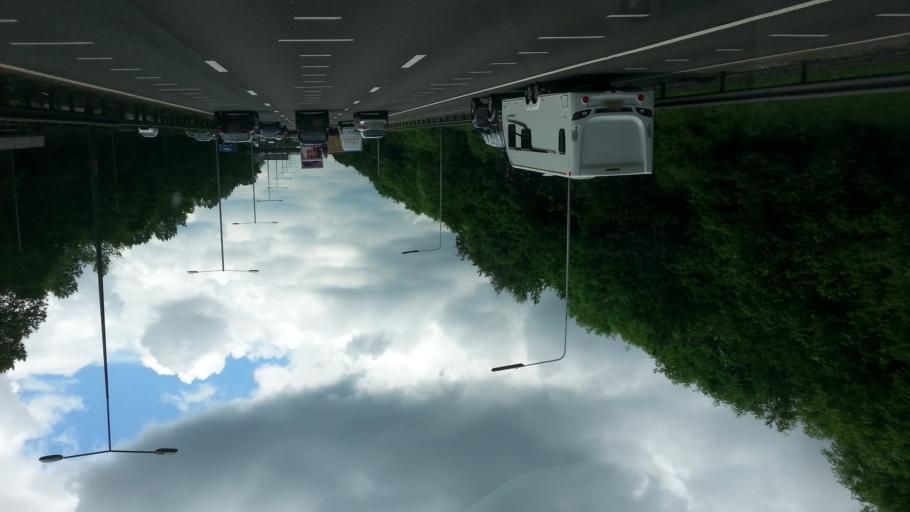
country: GB
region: England
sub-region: Staffordshire
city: Essington
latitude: 52.6249
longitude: -2.0415
